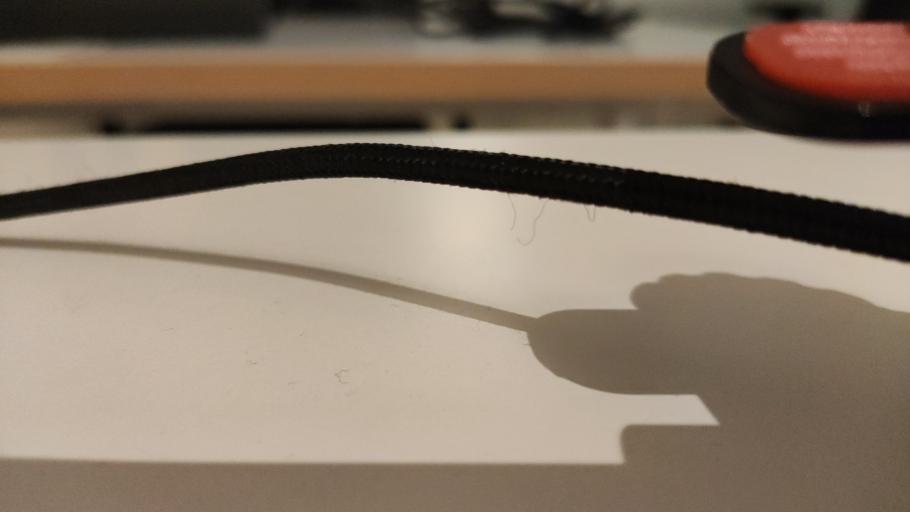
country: RU
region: Moskovskaya
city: Novoye
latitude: 55.6331
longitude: 38.9361
